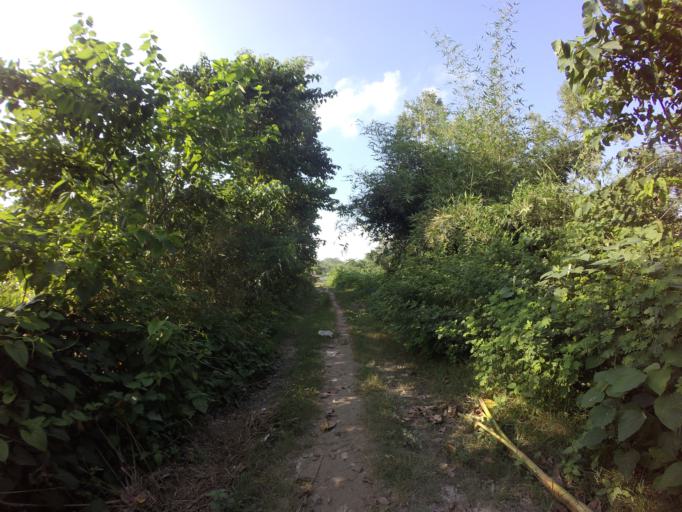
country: NP
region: Far Western
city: Tikapur
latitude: 28.4439
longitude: 81.0778
